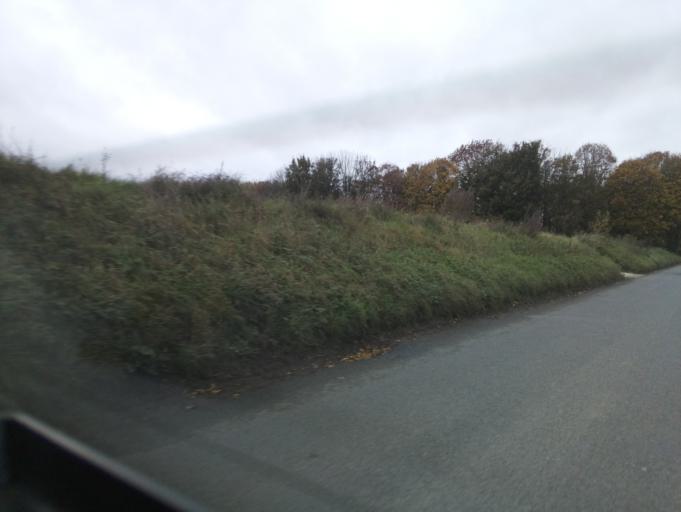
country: GB
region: England
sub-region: Somerset
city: South Petherton
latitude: 50.9393
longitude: -2.8427
